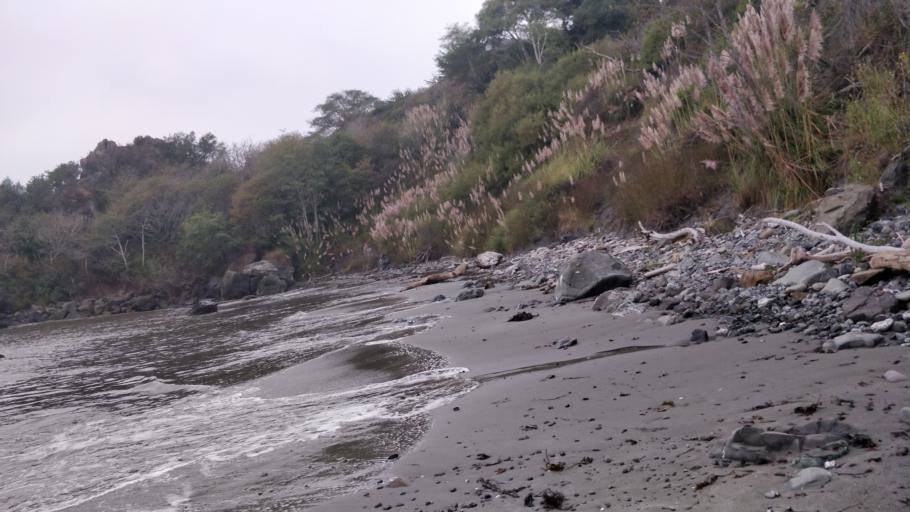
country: US
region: California
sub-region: Humboldt County
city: Westhaven-Moonstone
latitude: 41.0574
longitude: -124.1437
